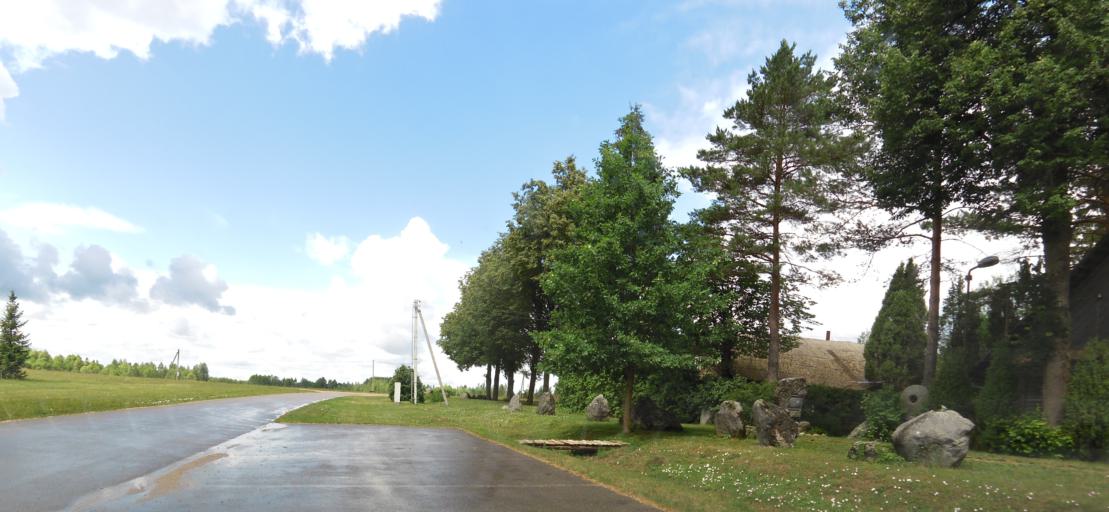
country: LT
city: Vabalninkas
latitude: 55.8868
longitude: 24.7766
